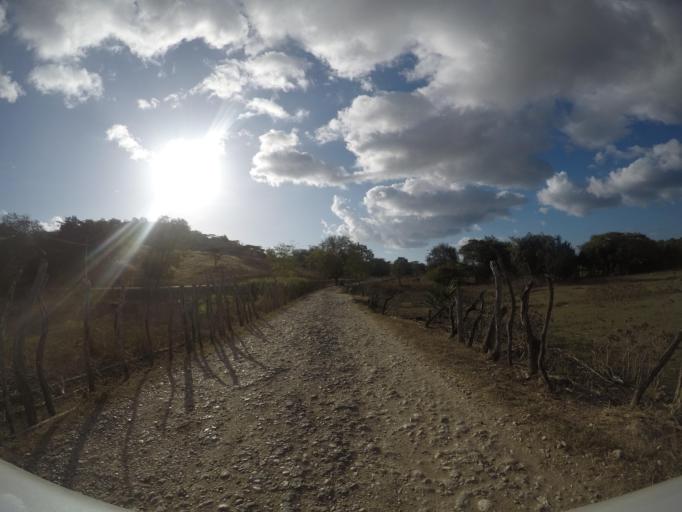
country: TL
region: Lautem
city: Lospalos
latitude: -8.4254
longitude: 126.8318
